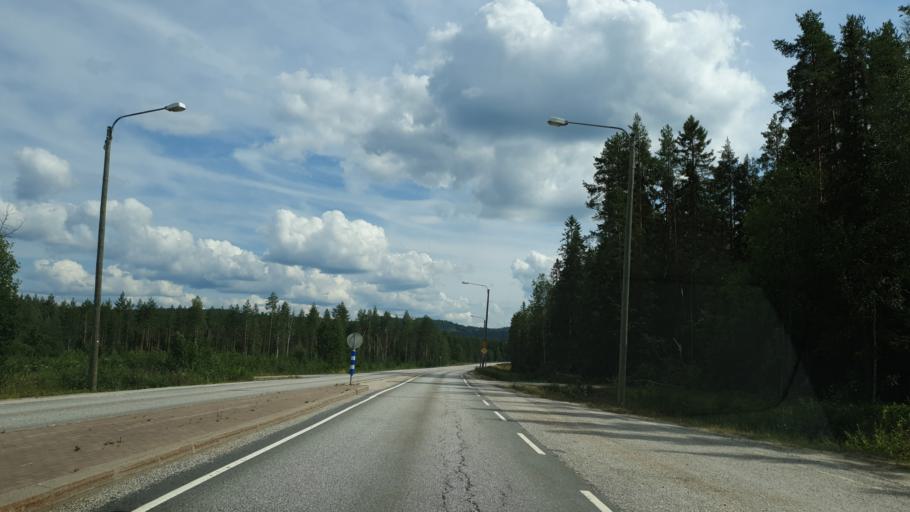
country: FI
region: Kainuu
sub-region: Kajaani
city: Vuokatti
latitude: 64.1154
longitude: 28.1753
